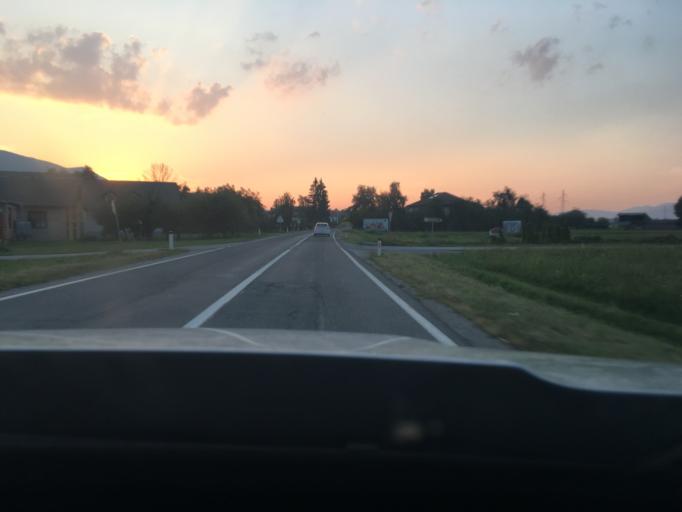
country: SI
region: Ribnica
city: Ribnica
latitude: 45.7109
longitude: 14.7526
